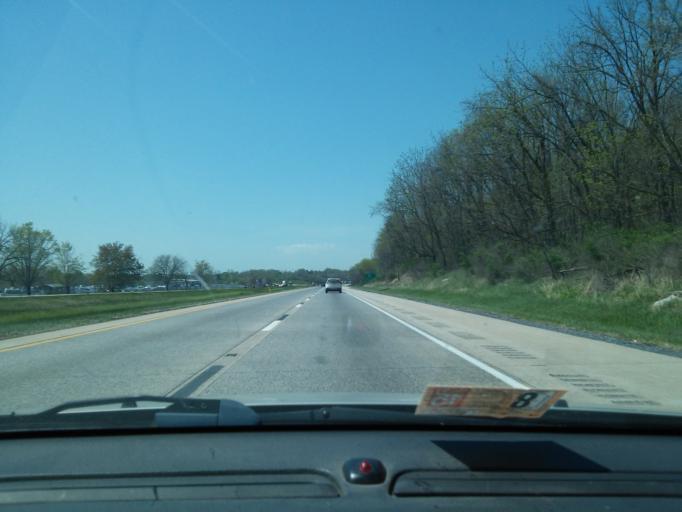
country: US
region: Pennsylvania
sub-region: Dauphin County
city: Skyline View
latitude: 40.3842
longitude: -76.6518
